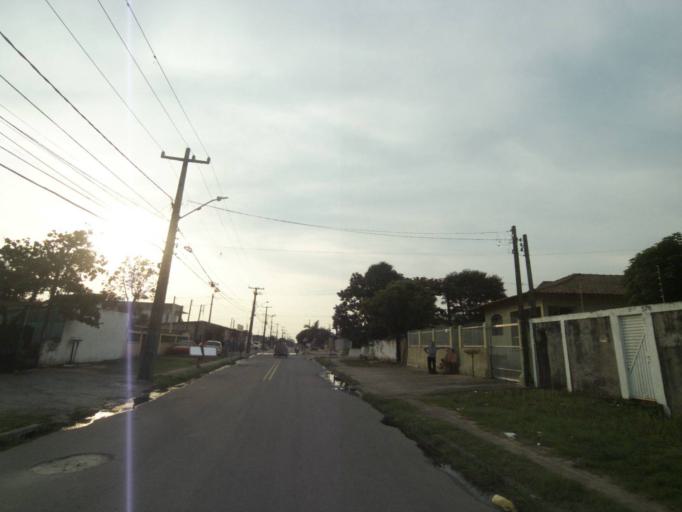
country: BR
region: Parana
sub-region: Paranagua
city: Paranagua
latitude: -25.5241
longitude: -48.5374
